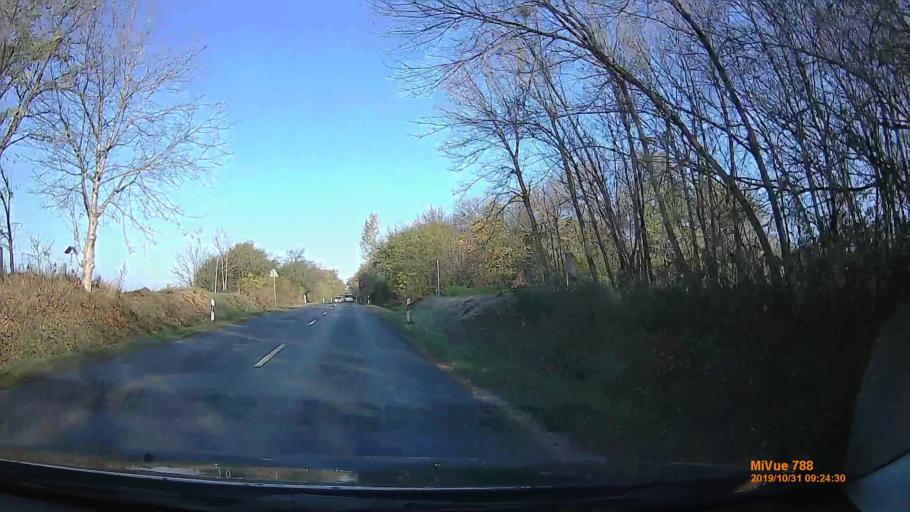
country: HU
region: Pest
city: Maglod
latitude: 47.4342
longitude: 19.3781
